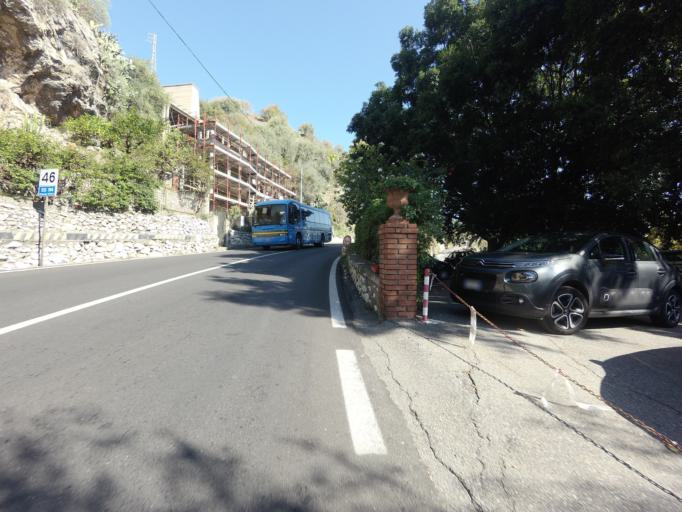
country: IT
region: Sicily
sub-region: Messina
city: Taormina
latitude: 37.8612
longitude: 15.2956
